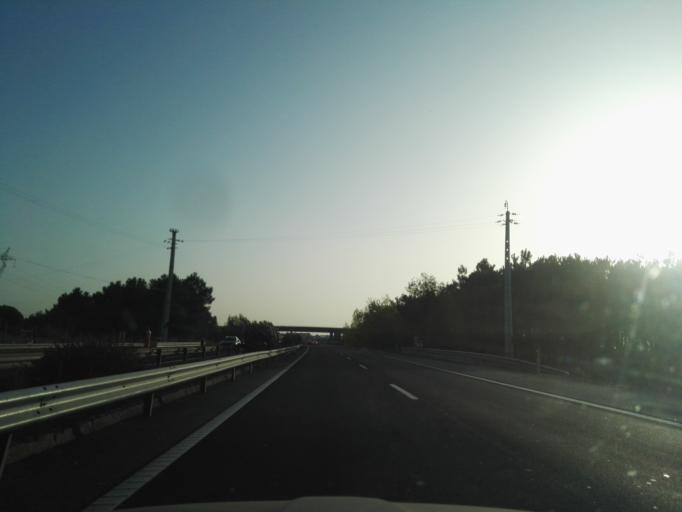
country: PT
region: Setubal
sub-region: Moita
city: Moita
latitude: 38.6616
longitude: -8.9599
